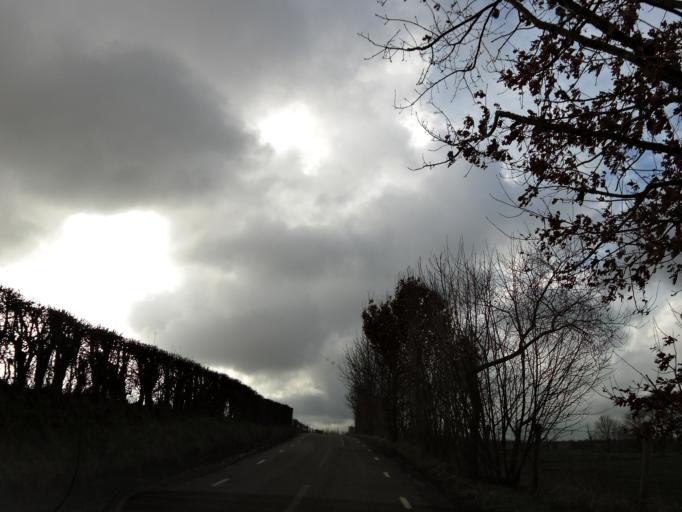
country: NL
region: Limburg
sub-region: Gemeente Maastricht
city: Heer
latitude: 50.8181
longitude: 5.7639
